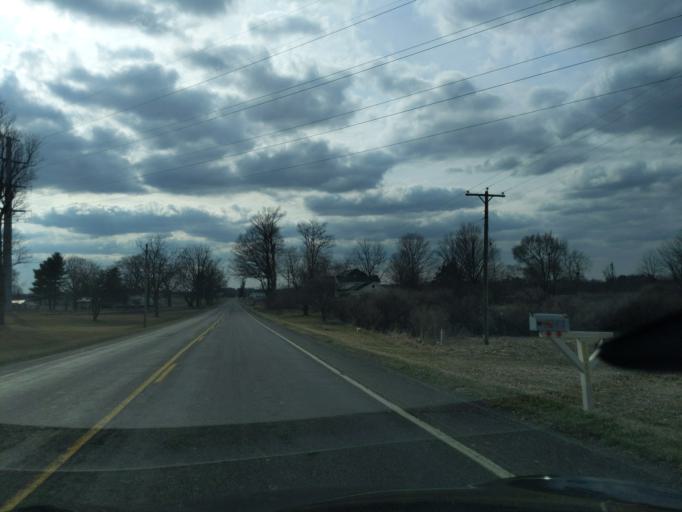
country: US
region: Michigan
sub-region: Ingham County
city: Mason
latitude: 42.5241
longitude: -84.4720
